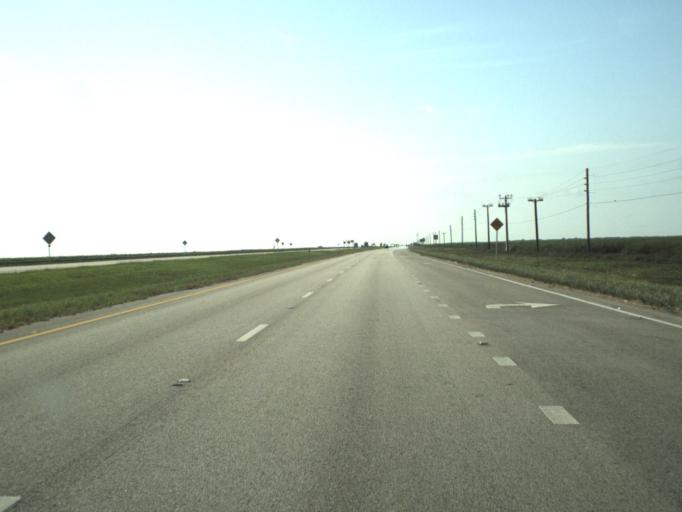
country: US
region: Florida
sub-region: Palm Beach County
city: Belle Glade Camp
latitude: 26.5508
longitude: -80.7056
